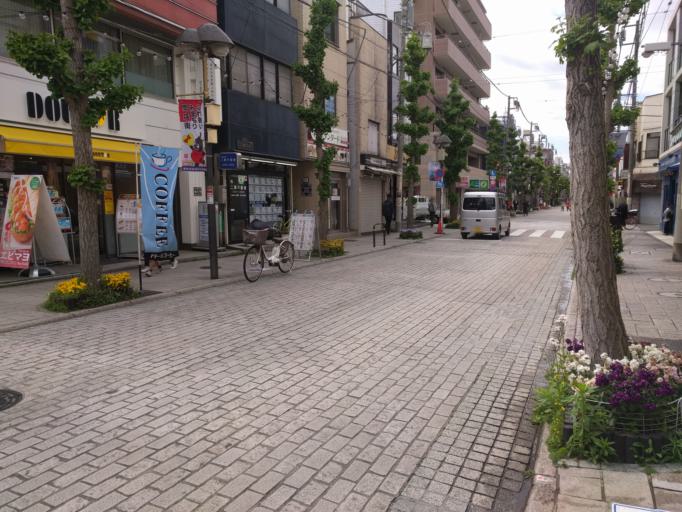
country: JP
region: Tokyo
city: Tokyo
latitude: 35.6070
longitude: 139.6533
